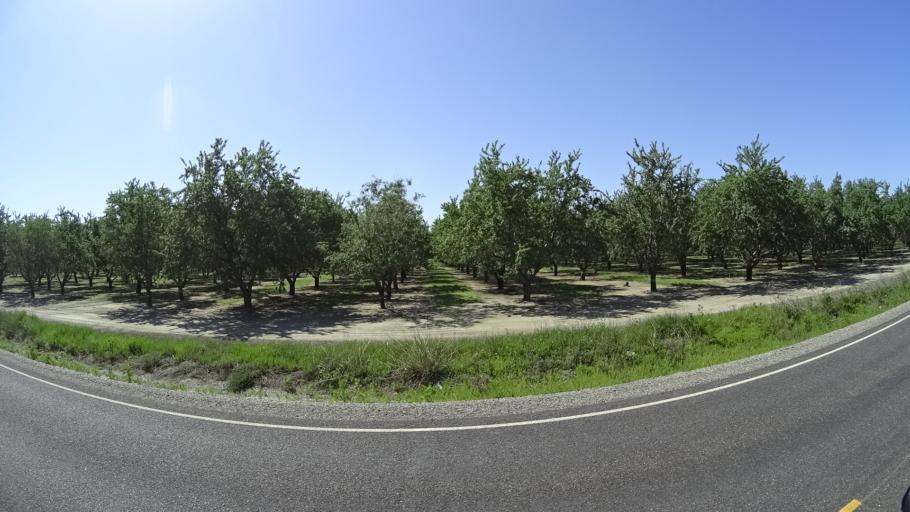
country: US
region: California
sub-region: Glenn County
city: Hamilton City
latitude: 39.7107
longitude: -122.0877
